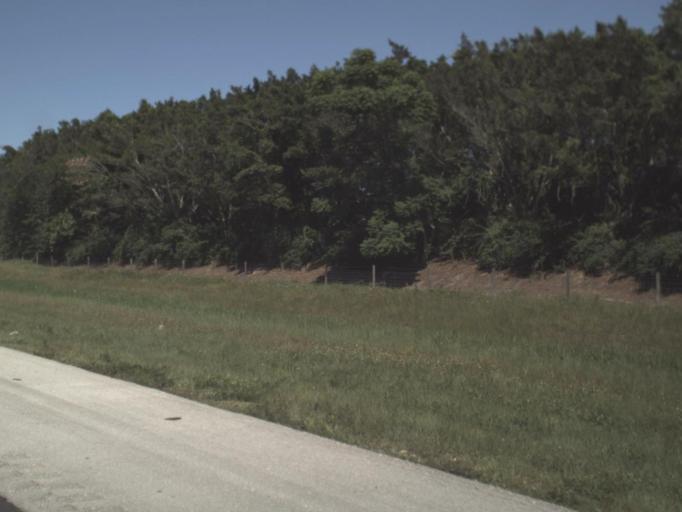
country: US
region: Florida
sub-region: Lee County
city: Three Oaks
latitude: 26.4722
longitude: -81.7906
